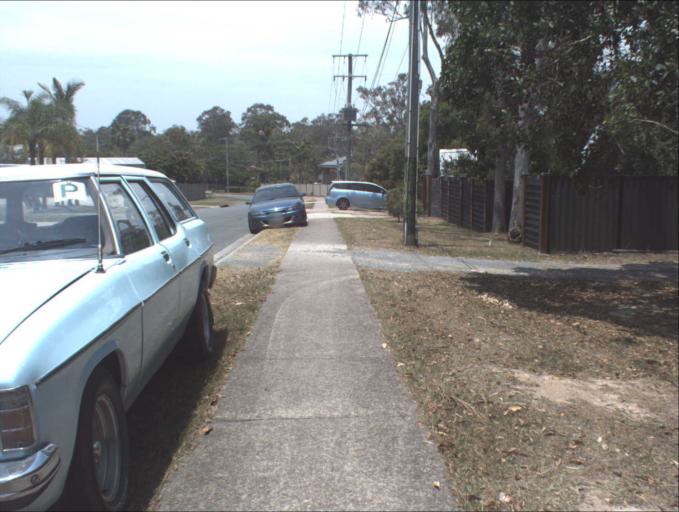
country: AU
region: Queensland
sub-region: Logan
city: Slacks Creek
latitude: -27.6686
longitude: 153.1841
